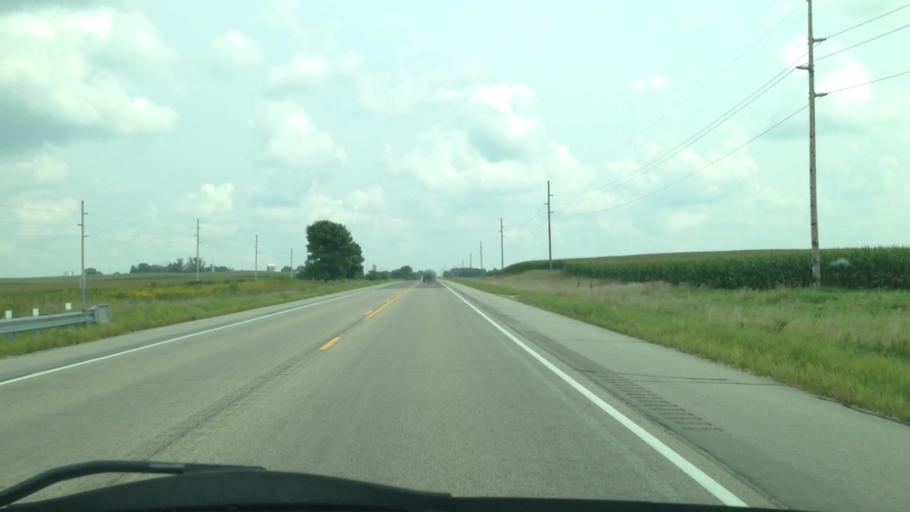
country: US
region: Minnesota
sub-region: Wabasha County
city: Elgin
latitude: 44.1414
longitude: -92.2352
